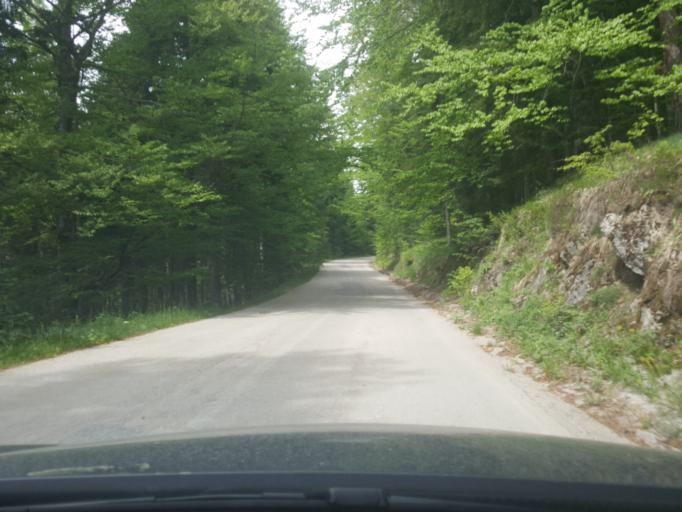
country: RS
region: Central Serbia
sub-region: Zlatiborski Okrug
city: Bajina Basta
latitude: 43.8902
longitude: 19.5264
